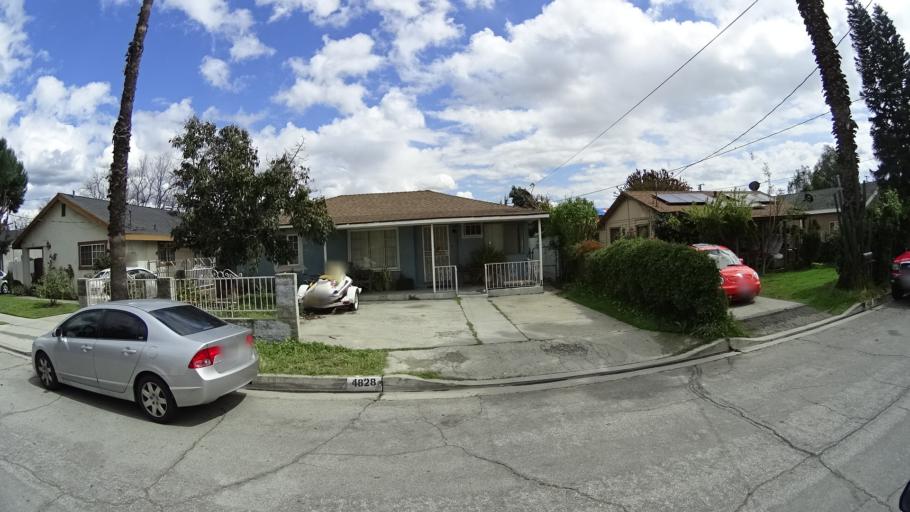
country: US
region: California
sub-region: Los Angeles County
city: Baldwin Park
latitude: 34.1005
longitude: -117.9594
